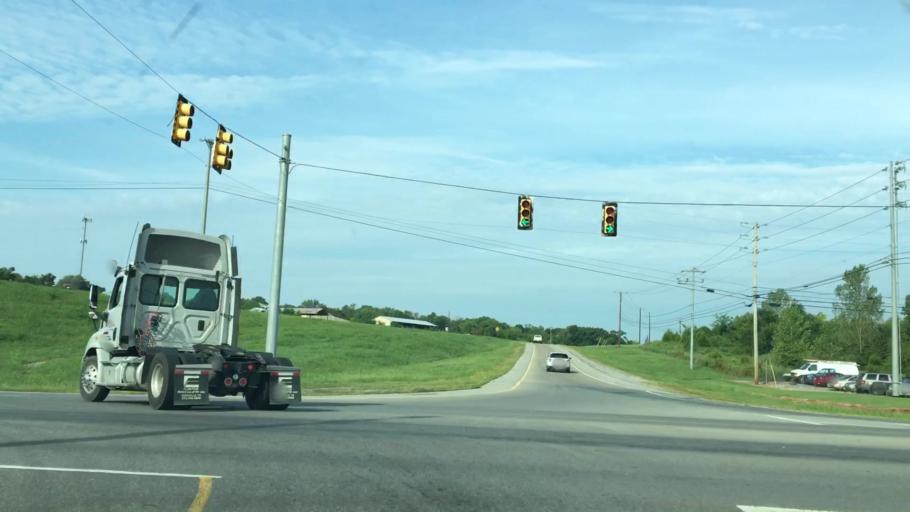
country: US
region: Tennessee
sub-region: Wilson County
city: Mount Juliet
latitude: 36.2337
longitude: -86.4290
